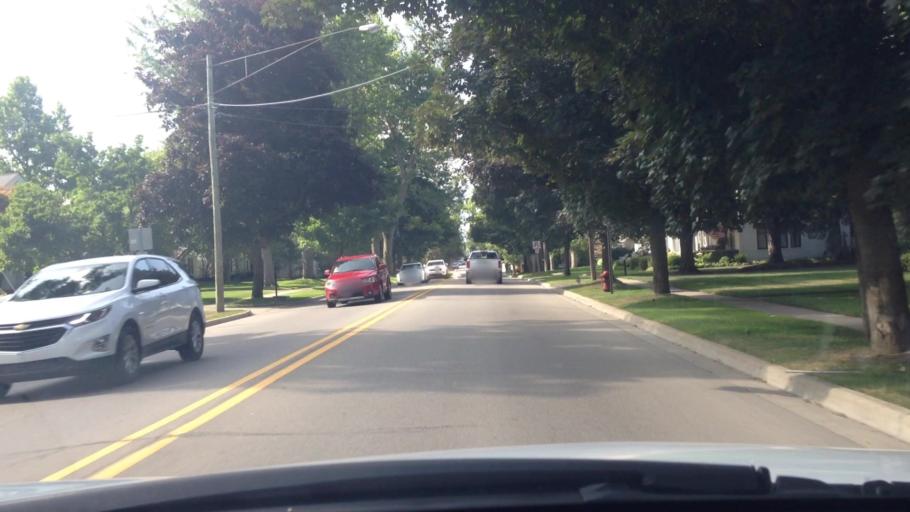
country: US
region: Michigan
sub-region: Oakland County
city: Clarkston
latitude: 42.7386
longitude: -83.4193
